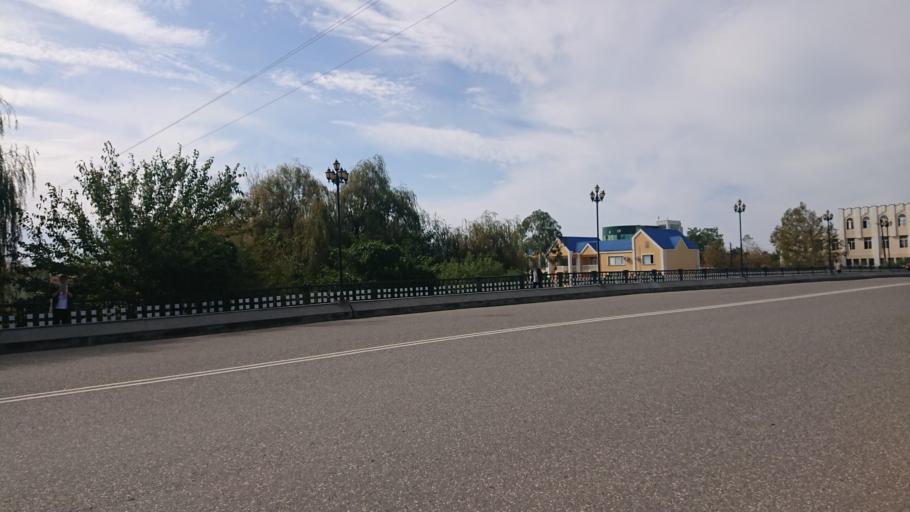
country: GE
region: Samegrelo and Zemo Svaneti
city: P'ot'i
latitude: 42.1434
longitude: 41.6728
